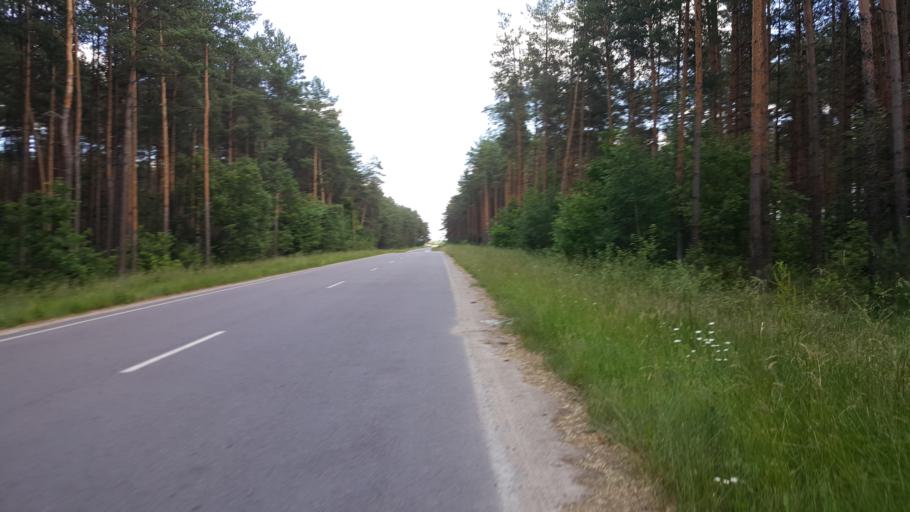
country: PL
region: Podlasie
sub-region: Powiat hajnowski
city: Czeremcha
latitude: 52.5408
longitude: 23.5183
